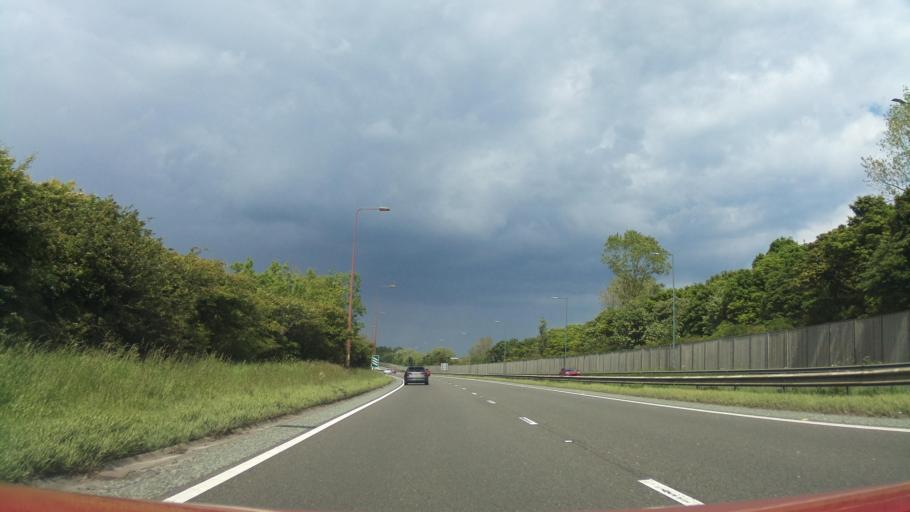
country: GB
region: England
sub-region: County Durham
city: Peterlee
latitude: 54.7547
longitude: -1.3602
